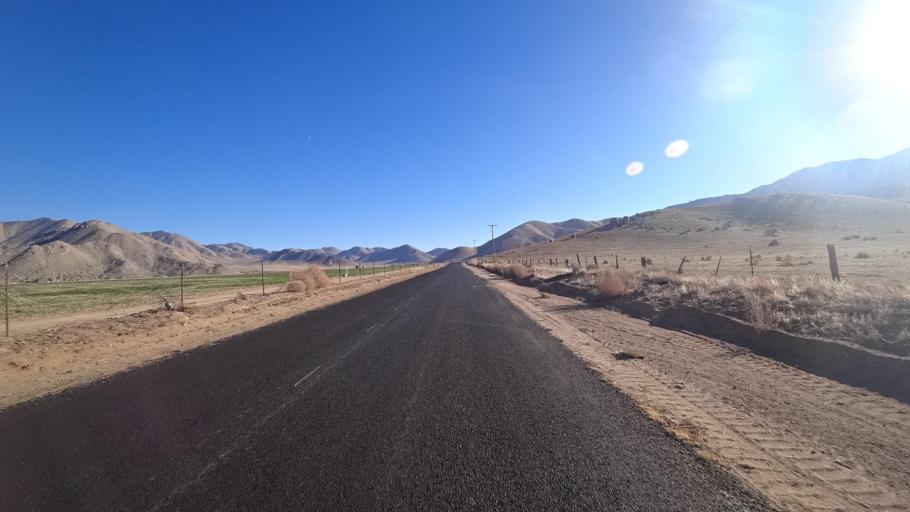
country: US
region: California
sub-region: Kern County
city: Weldon
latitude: 35.6342
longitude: -118.2640
